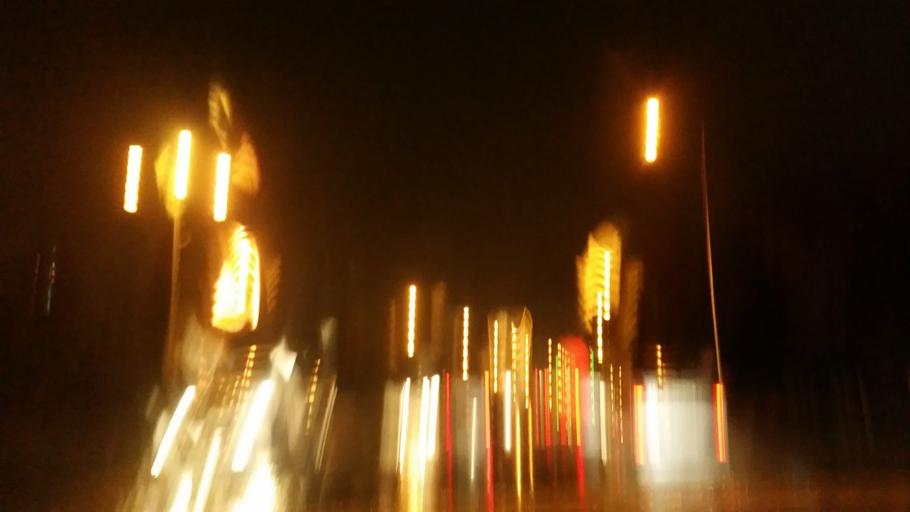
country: KZ
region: Astana Qalasy
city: Astana
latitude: 51.1651
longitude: 71.4748
